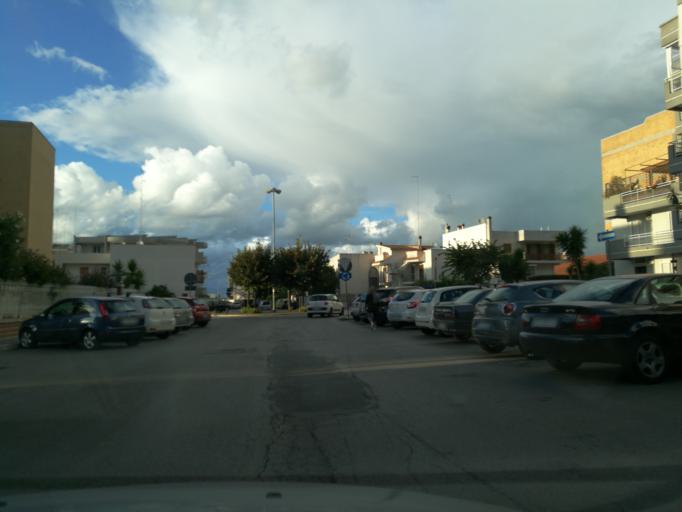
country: IT
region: Apulia
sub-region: Provincia di Bari
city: Valenzano
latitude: 41.0470
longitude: 16.8857
